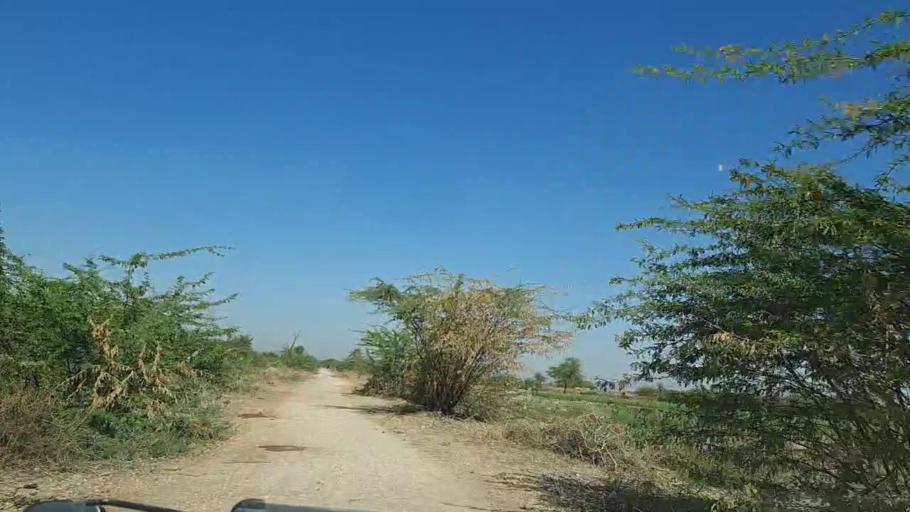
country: PK
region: Sindh
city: Dhoro Naro
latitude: 25.4621
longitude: 69.5136
